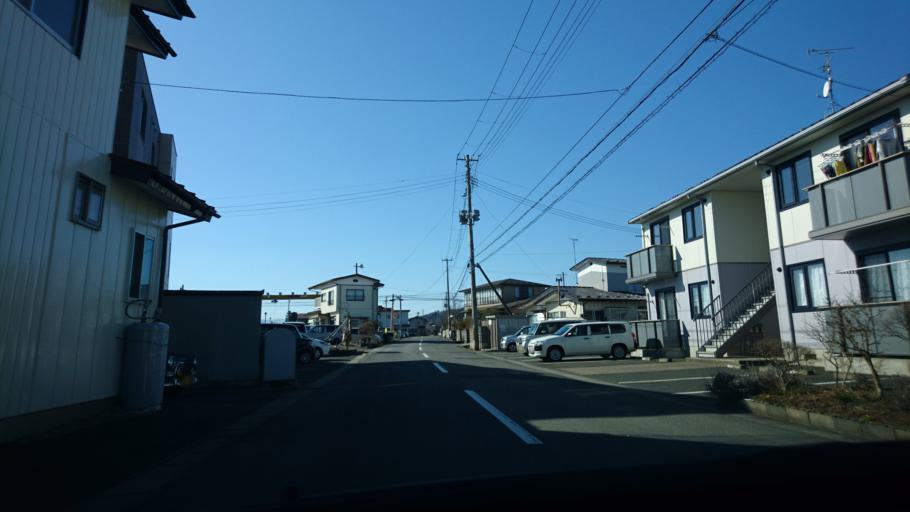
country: JP
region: Iwate
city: Ichinoseki
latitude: 38.9345
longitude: 141.1090
